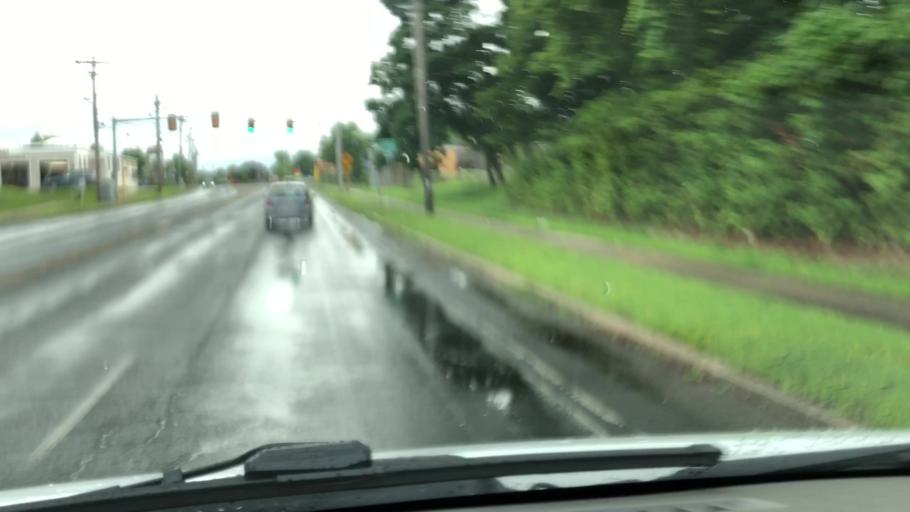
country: US
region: Massachusetts
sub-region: Hampshire County
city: Northampton
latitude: 42.3272
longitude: -72.6334
